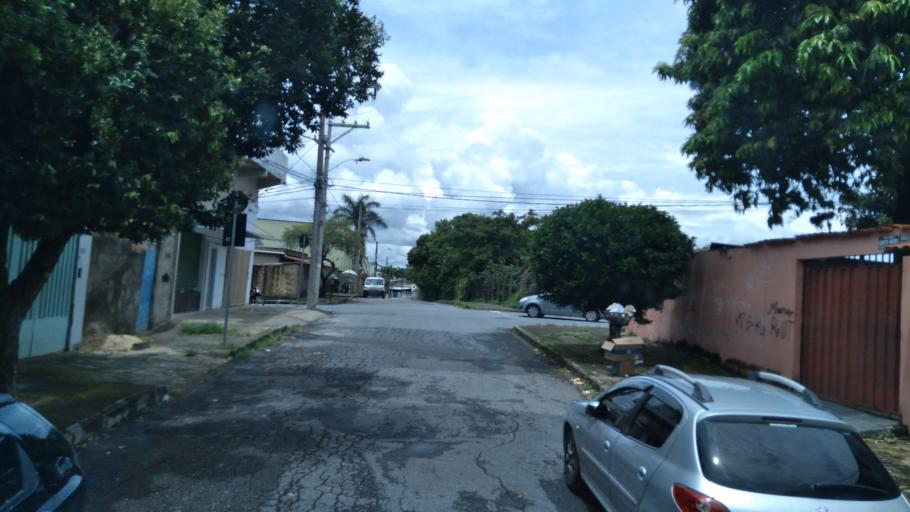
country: BR
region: Minas Gerais
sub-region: Belo Horizonte
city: Belo Horizonte
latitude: -19.8564
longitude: -43.9154
